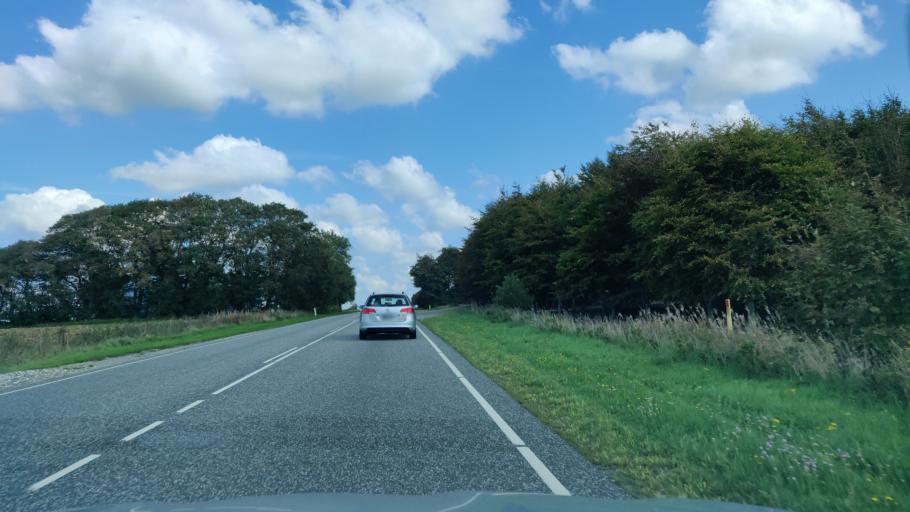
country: DK
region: North Denmark
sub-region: Vesthimmerland Kommune
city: Aars
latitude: 56.7948
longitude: 9.6218
